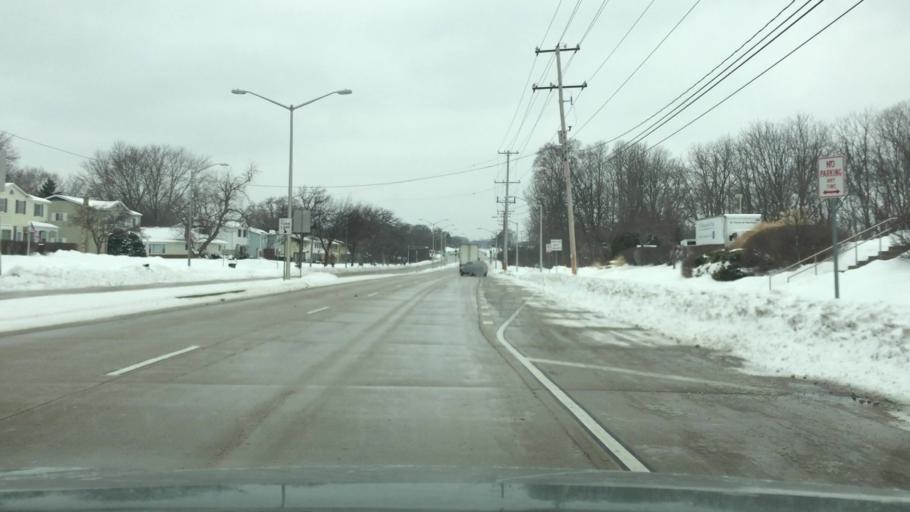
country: US
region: Wisconsin
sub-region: Waukesha County
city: Waukesha
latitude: 42.9885
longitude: -88.2603
